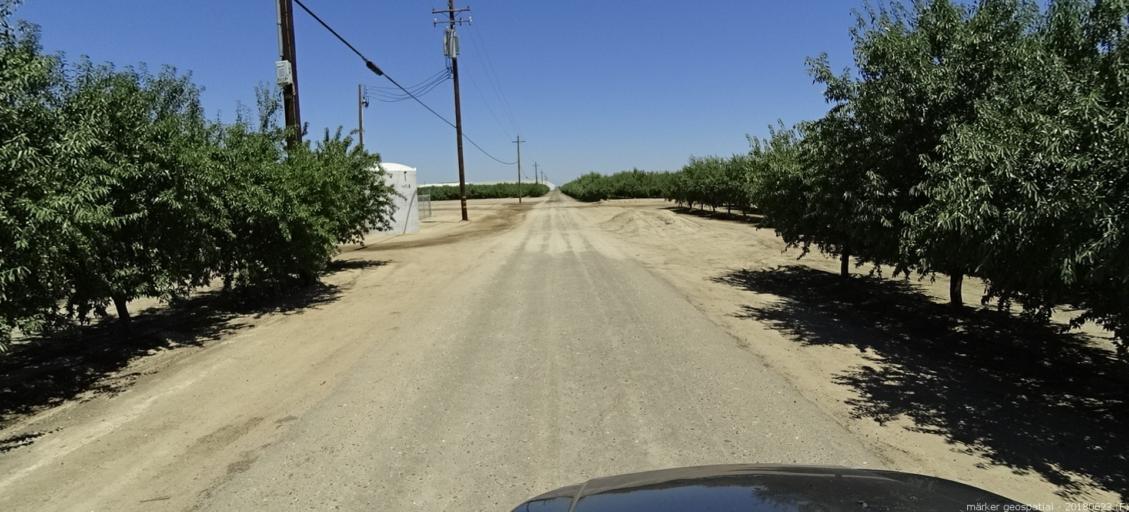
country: US
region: California
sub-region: Madera County
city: Fairmead
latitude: 37.0869
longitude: -120.2204
